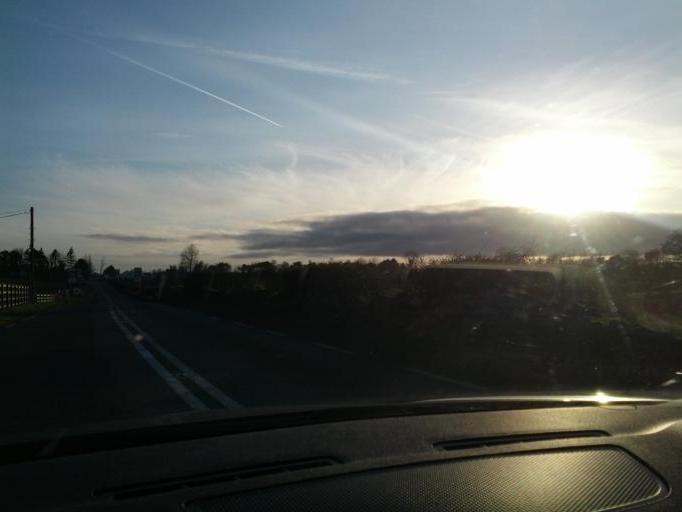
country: IE
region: Connaught
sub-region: Sligo
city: Tobercurry
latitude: 54.0616
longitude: -8.7153
